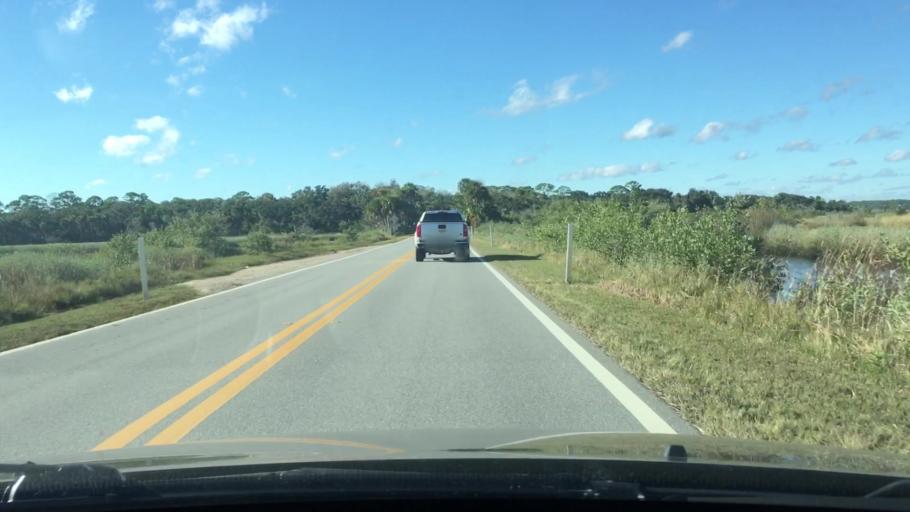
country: US
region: Florida
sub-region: Volusia County
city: Ormond-by-the-Sea
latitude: 29.3435
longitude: -81.0905
